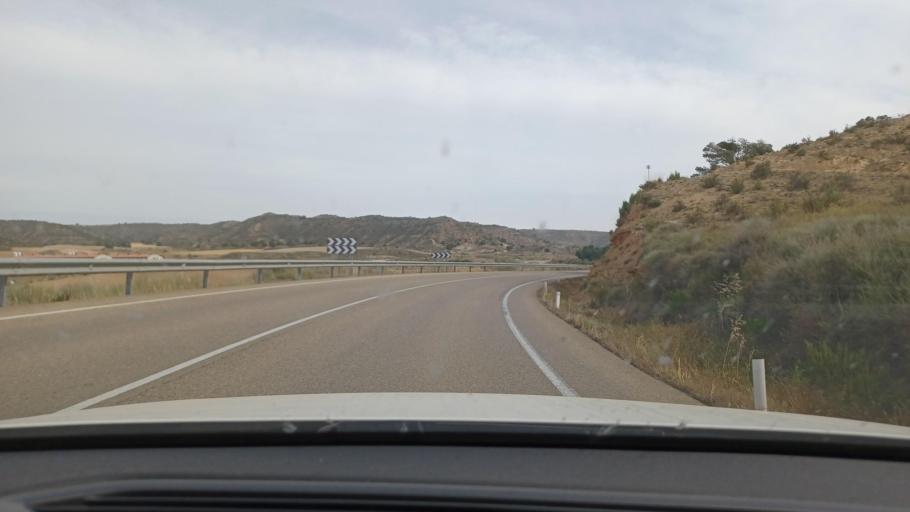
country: ES
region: Aragon
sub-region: Provincia de Zaragoza
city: Chiprana
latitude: 41.3323
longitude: -0.0893
